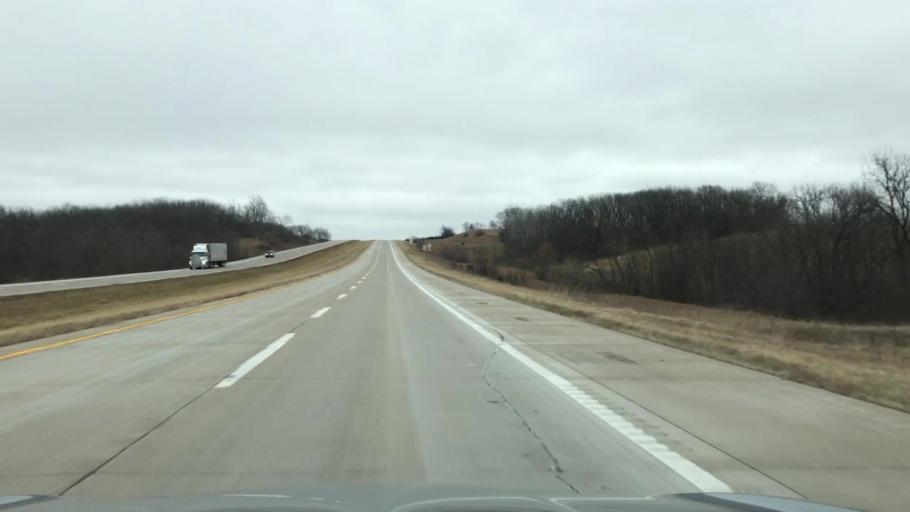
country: US
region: Missouri
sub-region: Livingston County
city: Chillicothe
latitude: 39.7354
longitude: -93.7537
